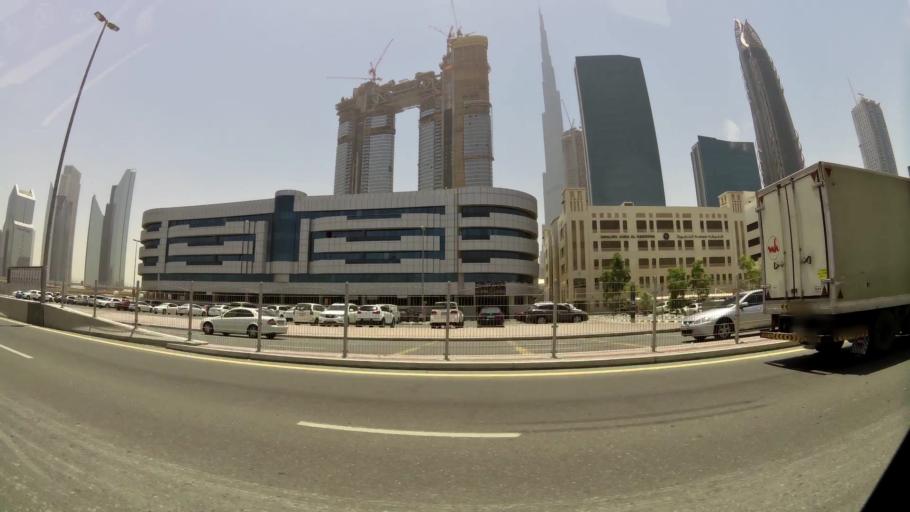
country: AE
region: Dubai
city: Dubai
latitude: 25.2028
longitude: 55.2668
